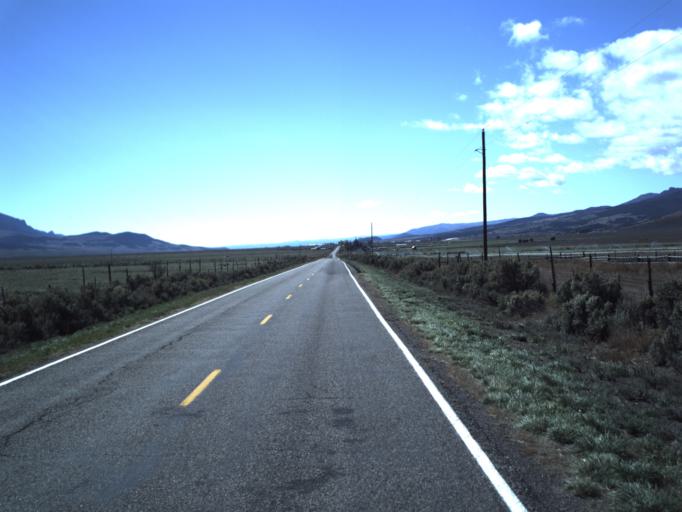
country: US
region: Utah
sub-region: Sevier County
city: Monroe
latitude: 38.4671
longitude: -111.9068
